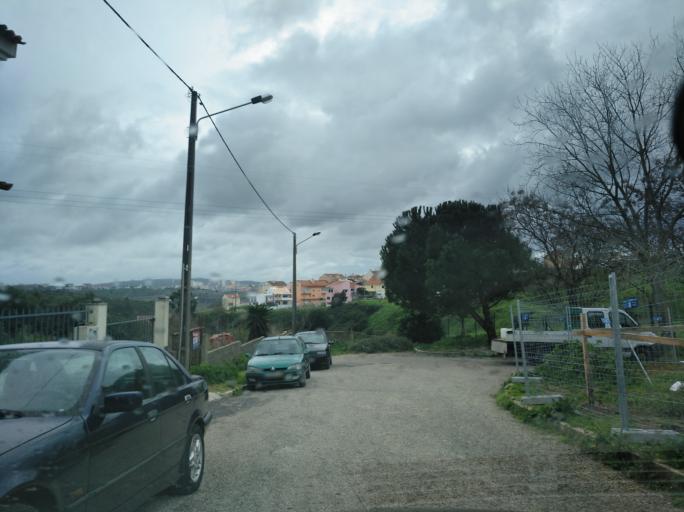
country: PT
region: Lisbon
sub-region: Odivelas
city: Famoes
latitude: 38.7882
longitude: -9.2042
